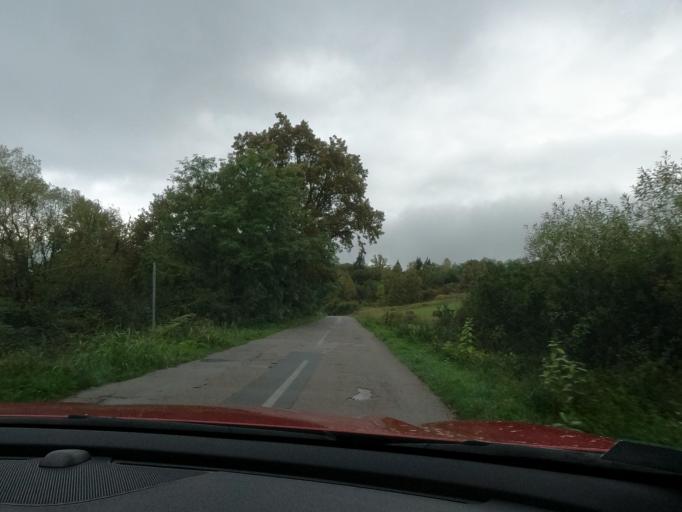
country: HR
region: Sisacko-Moslavacka
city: Glina
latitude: 45.2972
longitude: 16.1427
